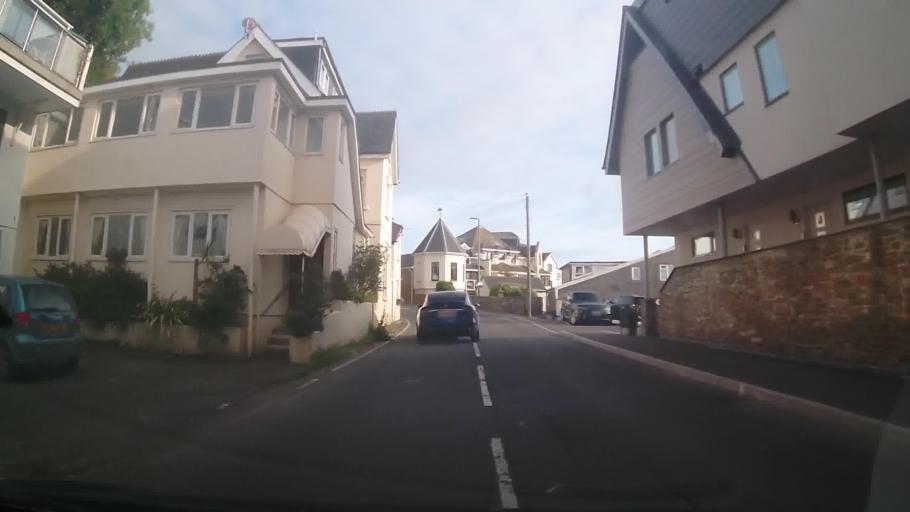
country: GB
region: England
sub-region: Devon
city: Kingsbridge
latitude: 50.2767
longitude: -3.7722
